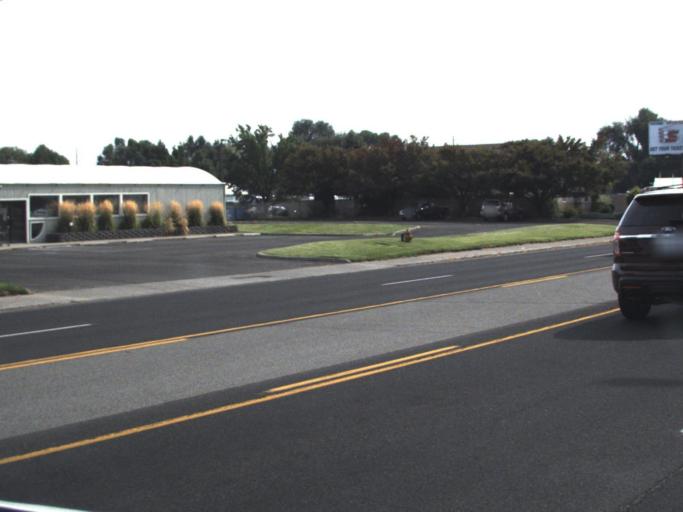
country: US
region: Washington
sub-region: Spokane County
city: Country Homes
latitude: 47.7489
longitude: -117.4113
